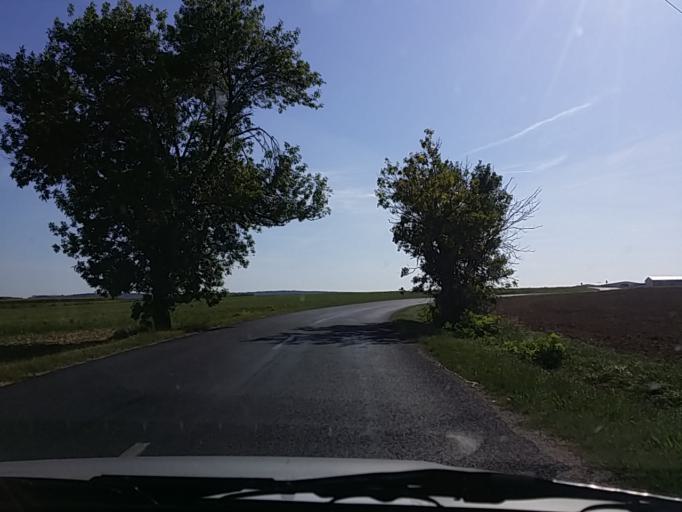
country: AT
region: Burgenland
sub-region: Politischer Bezirk Oberpullendorf
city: Lutzmannsburg
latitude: 47.4331
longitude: 16.6580
